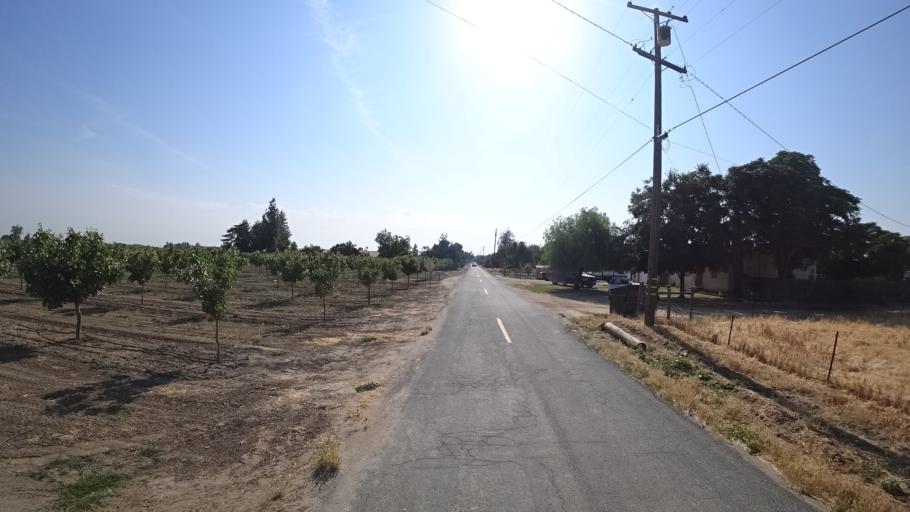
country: US
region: California
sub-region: Kings County
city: Lemoore
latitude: 36.3531
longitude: -119.8417
